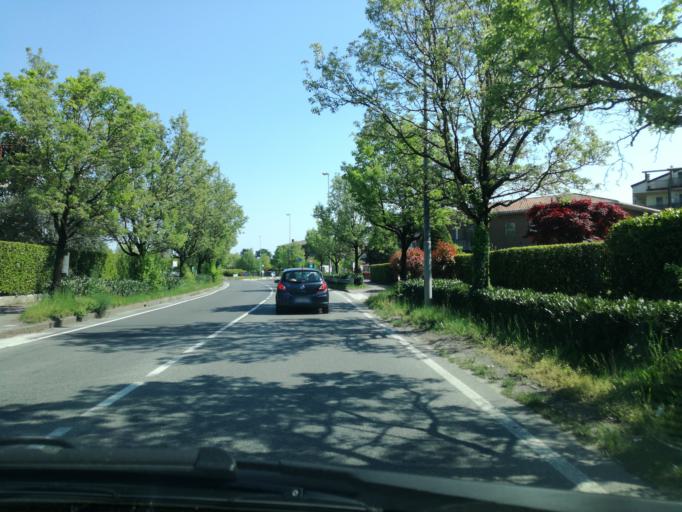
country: IT
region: Lombardy
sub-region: Provincia di Bergamo
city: Terno d'Isola
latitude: 45.6870
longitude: 9.5305
